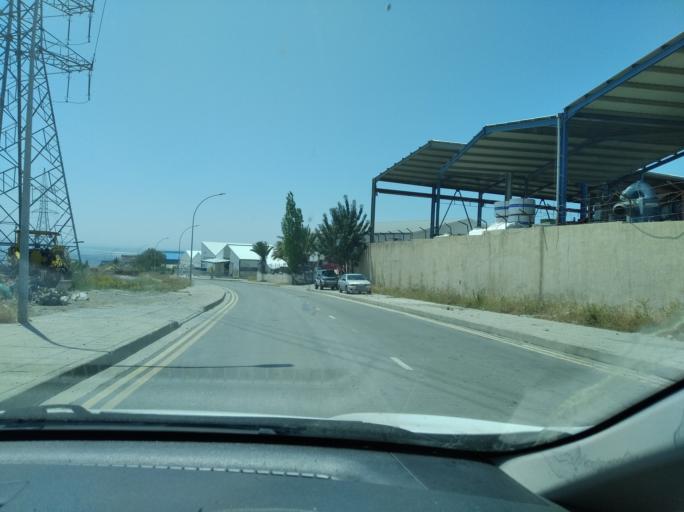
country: CY
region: Limassol
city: Ypsonas
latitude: 34.7334
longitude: 32.9443
